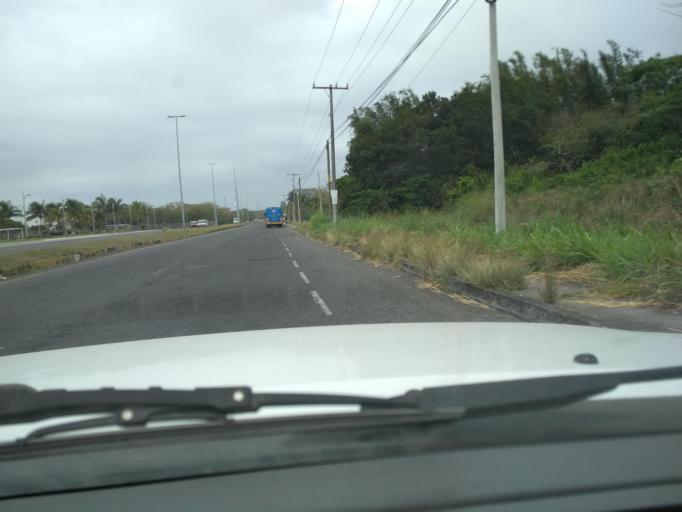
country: MX
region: Veracruz
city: Boca del Rio
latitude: 19.0939
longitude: -96.1107
